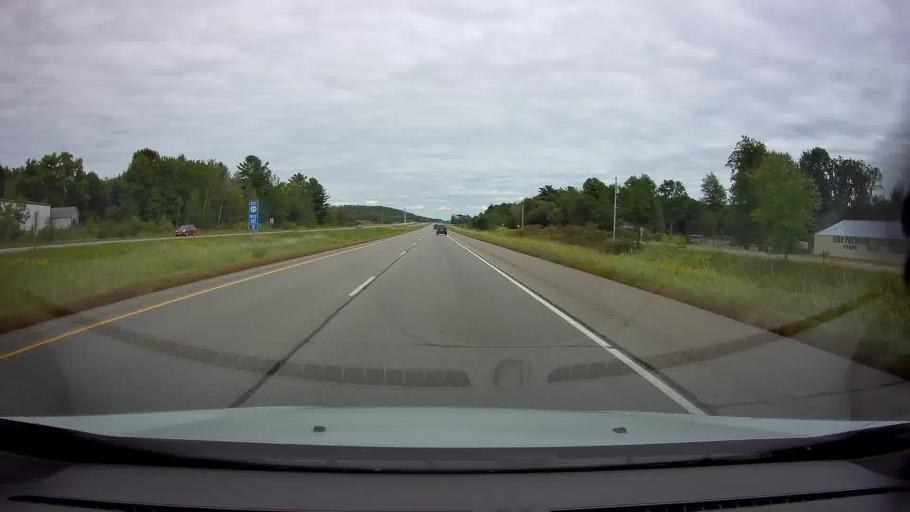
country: US
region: Wisconsin
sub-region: Marathon County
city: Rib Mountain
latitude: 44.9502
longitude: -89.7409
